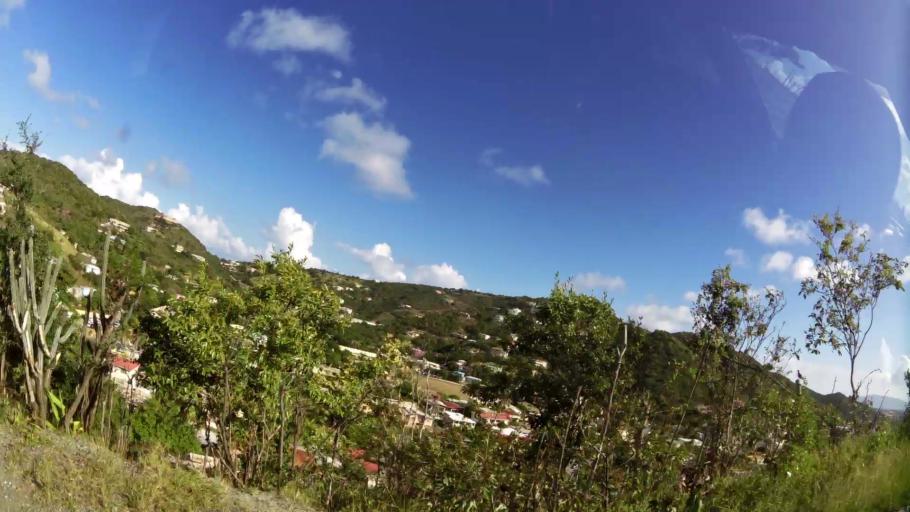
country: VG
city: Tortola
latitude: 18.4366
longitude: -64.5729
